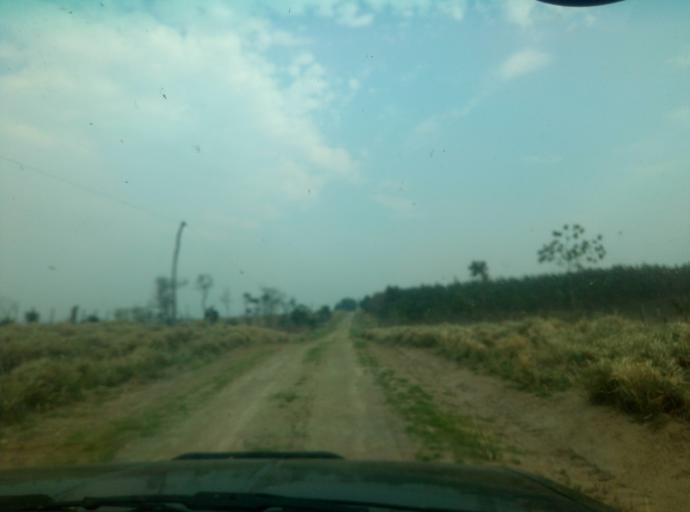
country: PY
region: Caaguazu
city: San Joaquin
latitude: -25.1078
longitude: -56.1276
